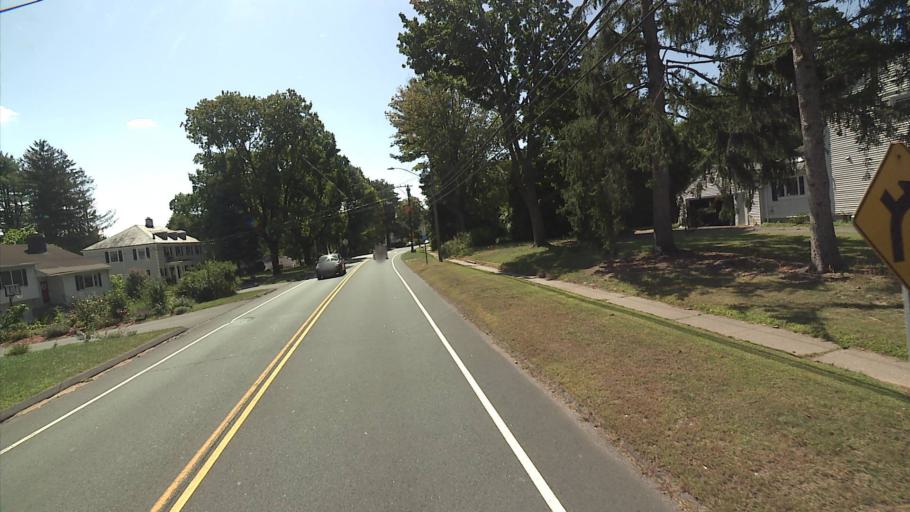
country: US
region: Connecticut
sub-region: Hartford County
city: West Hartford
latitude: 41.7936
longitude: -72.7467
